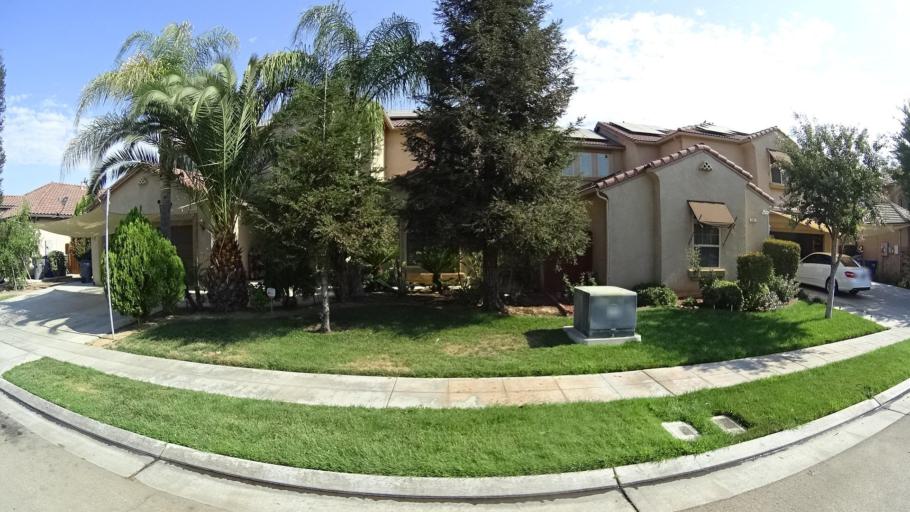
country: US
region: California
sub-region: Fresno County
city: Sunnyside
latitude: 36.7103
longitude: -119.6881
